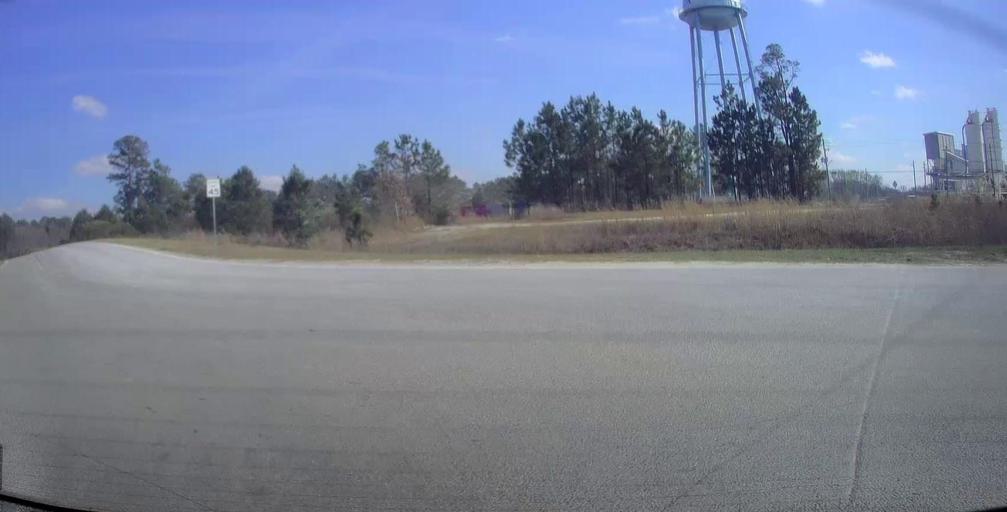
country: US
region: Georgia
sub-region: Wilkinson County
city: Gordon
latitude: 32.8940
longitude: -83.3102
